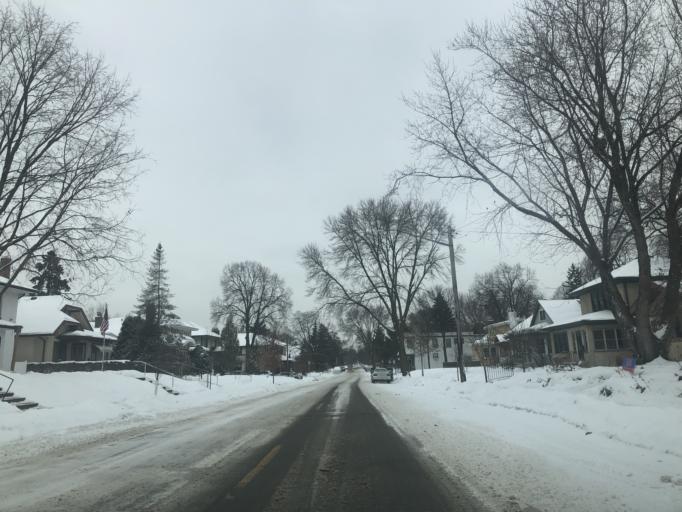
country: US
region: Minnesota
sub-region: Hennepin County
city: Richfield
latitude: 44.9296
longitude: -93.2844
